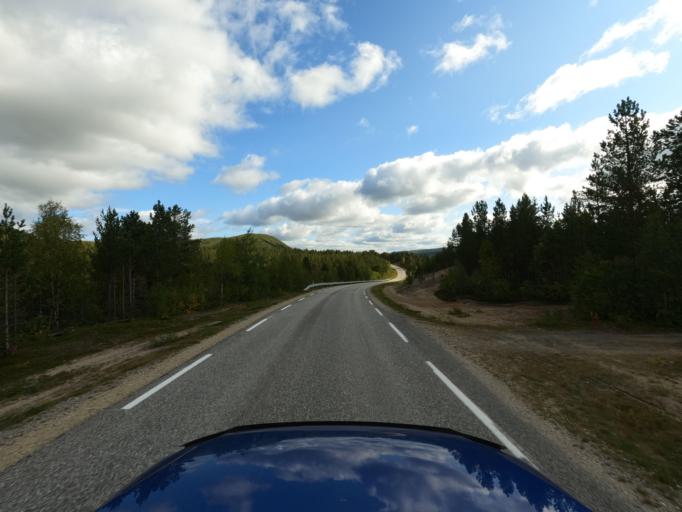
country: NO
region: Finnmark Fylke
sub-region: Karasjok
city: Karasjohka
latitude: 69.4430
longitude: 25.2665
